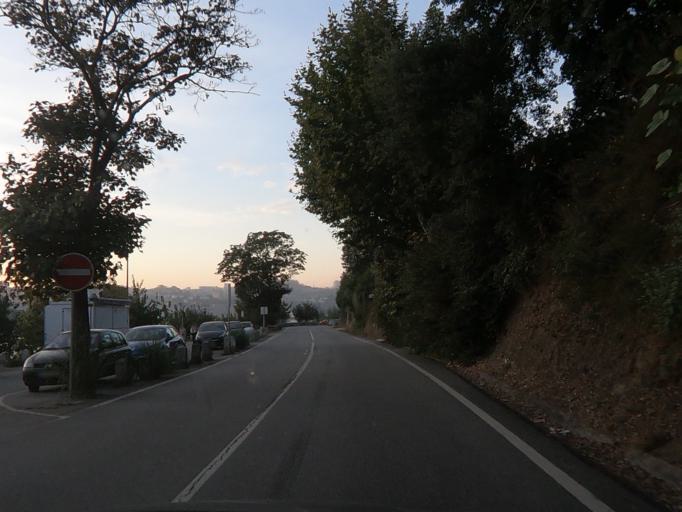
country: PT
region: Porto
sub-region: Gondomar
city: Valbom
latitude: 41.1313
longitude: -8.5686
